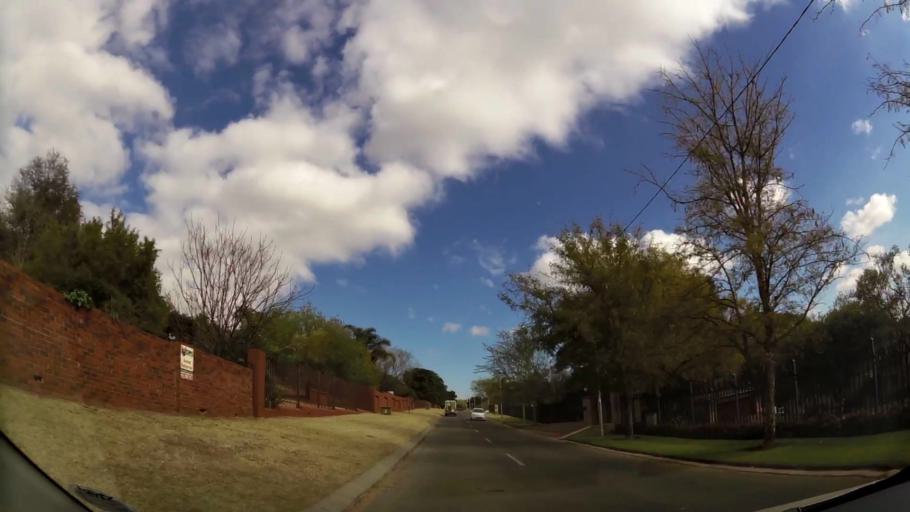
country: ZA
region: Gauteng
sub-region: West Rand District Municipality
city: Muldersdriseloop
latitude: -26.0930
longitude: 27.8544
